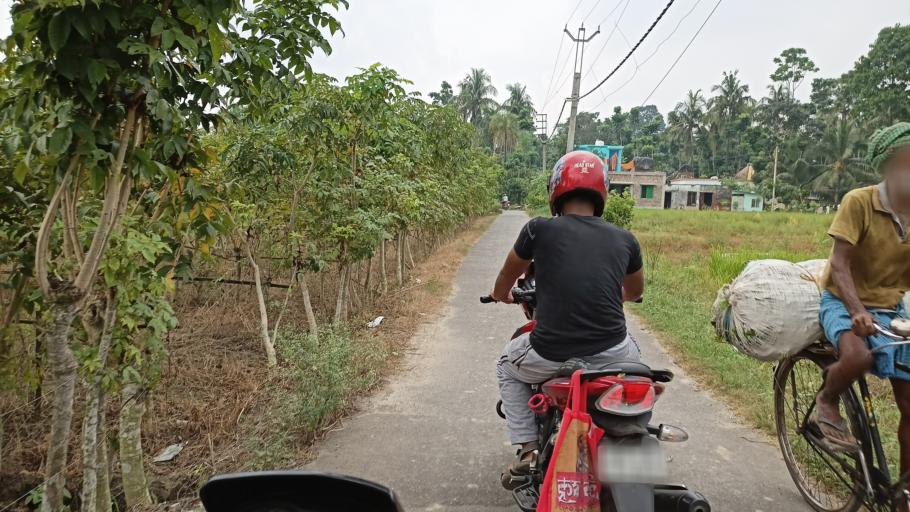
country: IN
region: West Bengal
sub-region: North 24 Parganas
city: Bangaon
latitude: 23.0638
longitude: 88.8191
